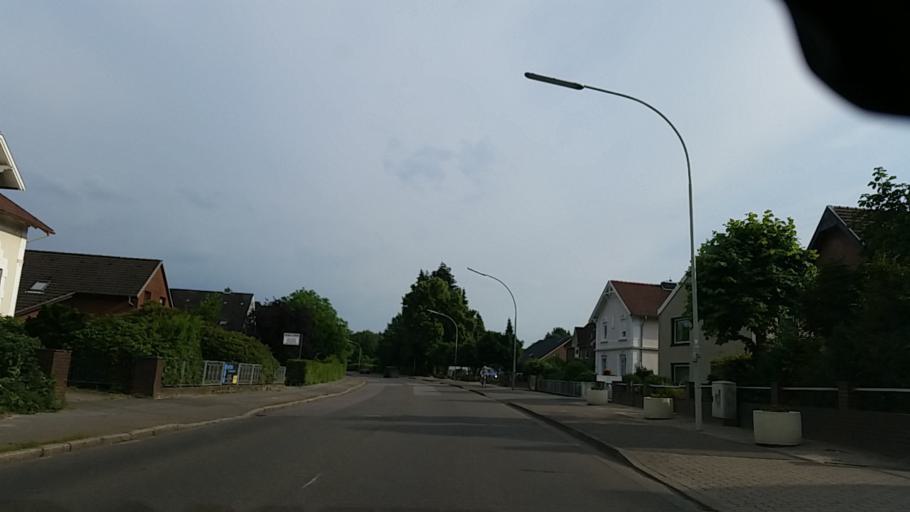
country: DE
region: Schleswig-Holstein
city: Halstenbek
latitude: 53.5951
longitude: 9.8222
